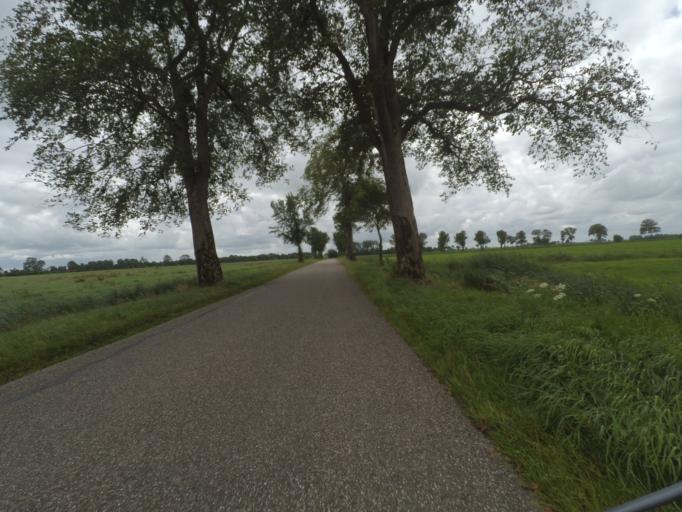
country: NL
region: Friesland
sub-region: Gemeente Kollumerland en Nieuwkruisland
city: Kollumerzwaag
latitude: 53.3003
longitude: 6.0872
